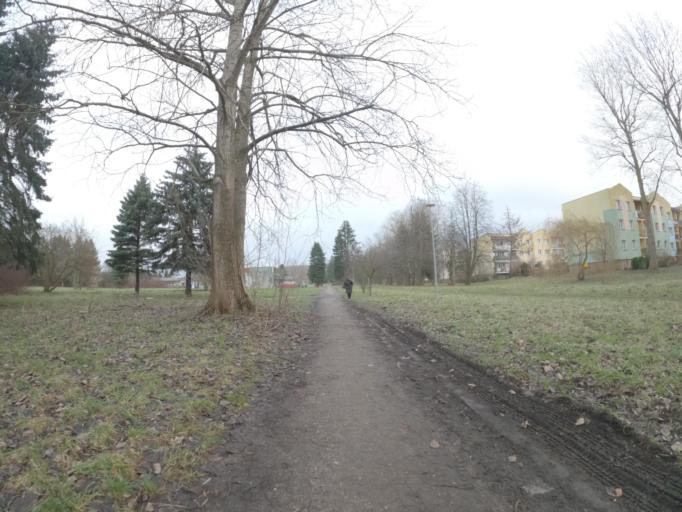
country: PL
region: West Pomeranian Voivodeship
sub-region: Koszalin
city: Koszalin
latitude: 54.2009
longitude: 16.2050
